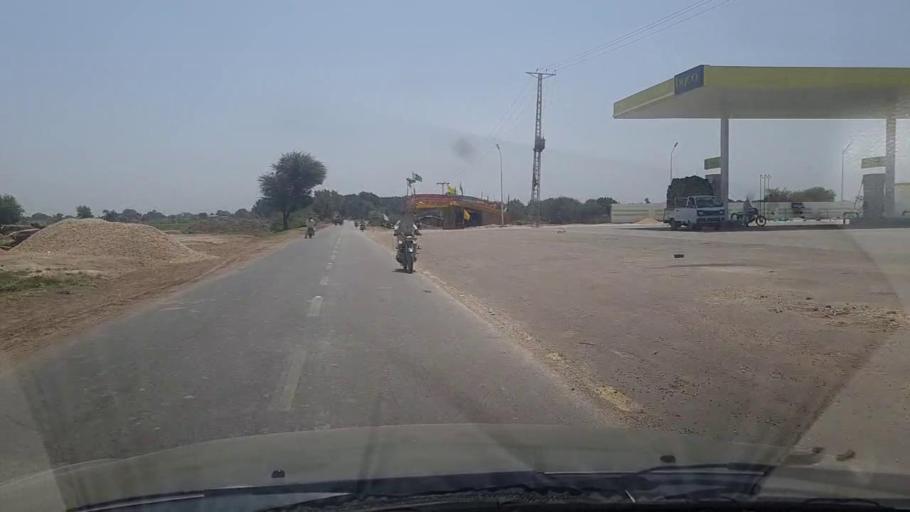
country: PK
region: Sindh
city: Tando Jam
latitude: 25.3147
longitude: 68.5640
